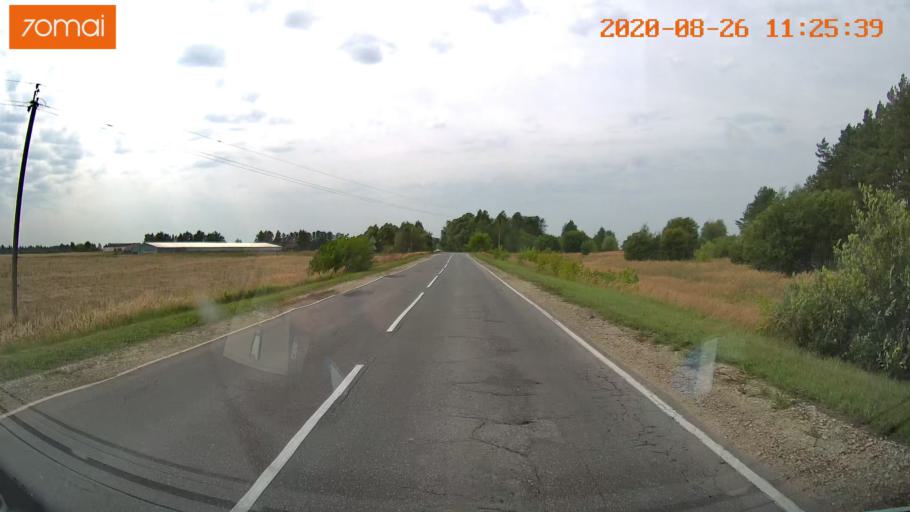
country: RU
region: Rjazan
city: Shilovo
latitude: 54.3402
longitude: 40.9605
